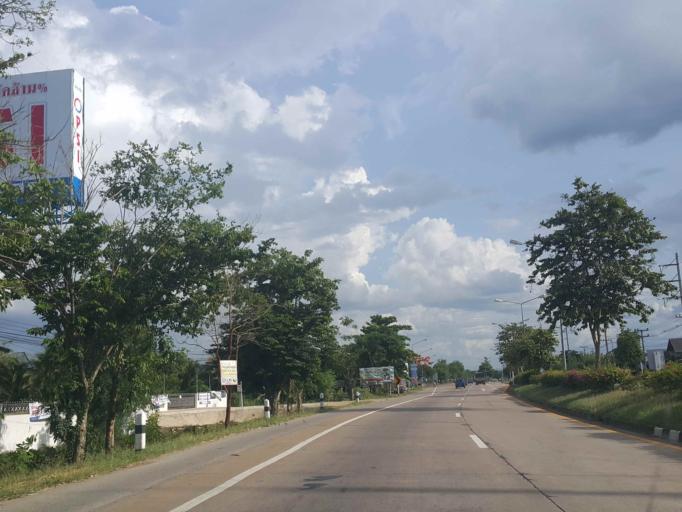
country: TH
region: Phrae
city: Sung Men
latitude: 18.0247
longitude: 100.1109
